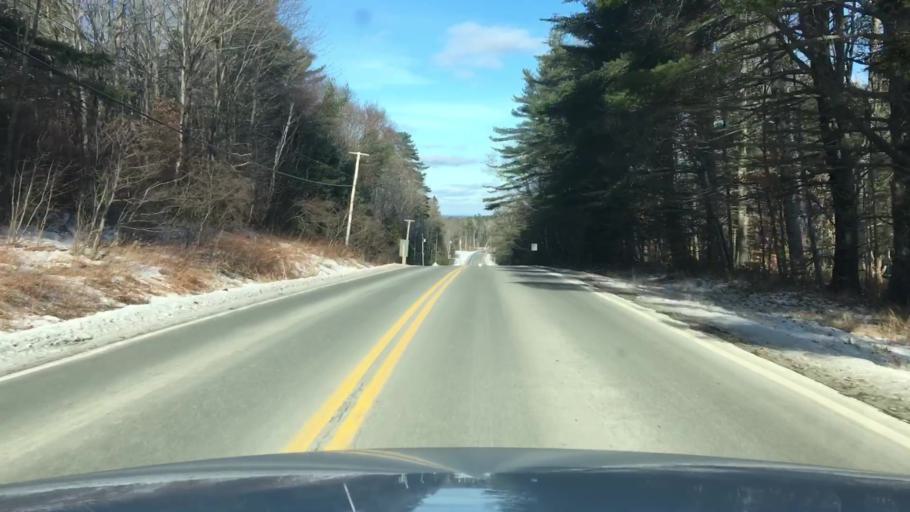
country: US
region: Maine
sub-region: Penobscot County
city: Holden
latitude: 44.7458
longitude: -68.6150
